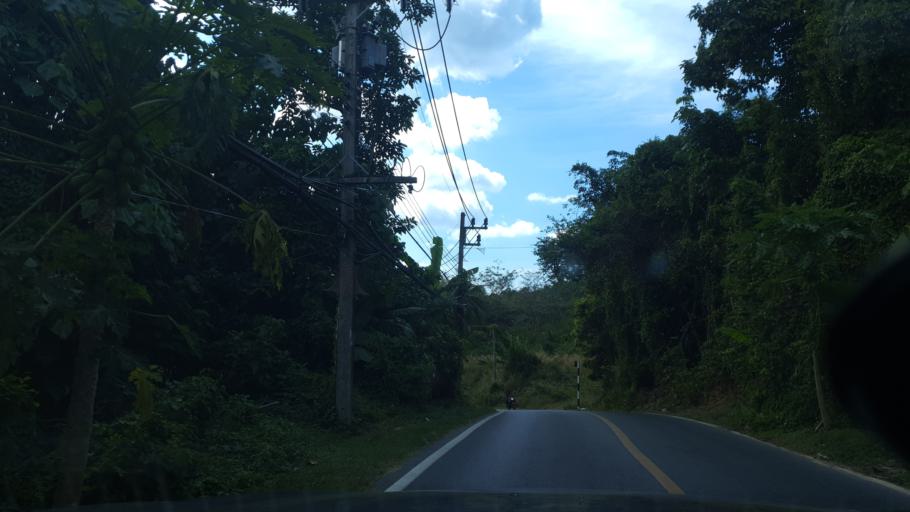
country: TH
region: Phuket
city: Thalang
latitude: 8.0640
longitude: 98.2802
